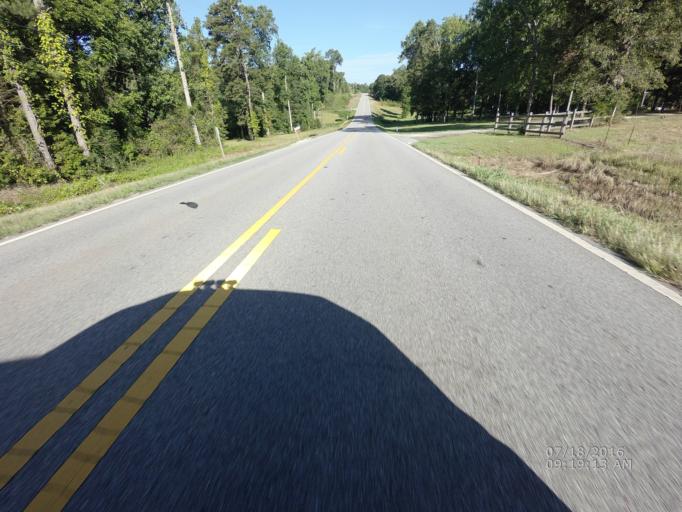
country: US
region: Alabama
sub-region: Chambers County
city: Huguley
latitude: 32.8633
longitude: -85.2922
